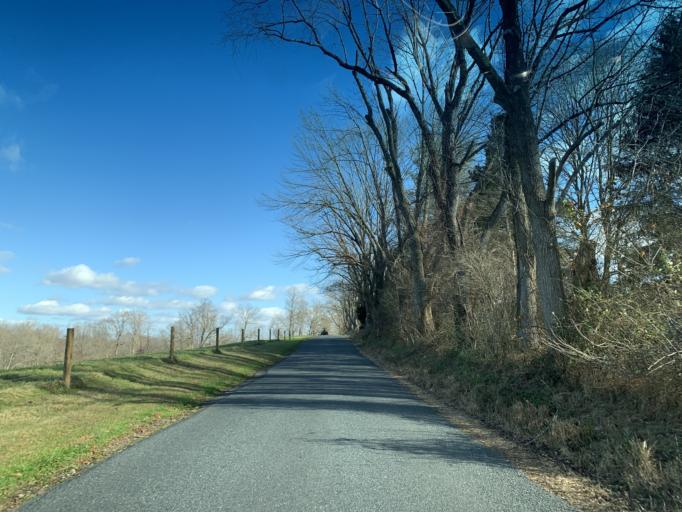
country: US
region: Maryland
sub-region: Harford County
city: Aberdeen
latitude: 39.5853
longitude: -76.2367
